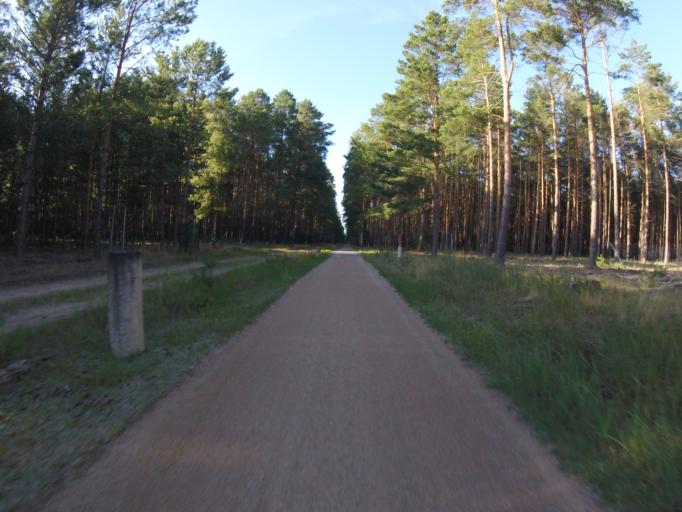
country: DE
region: Brandenburg
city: Munchehofe
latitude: 52.1970
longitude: 13.7644
